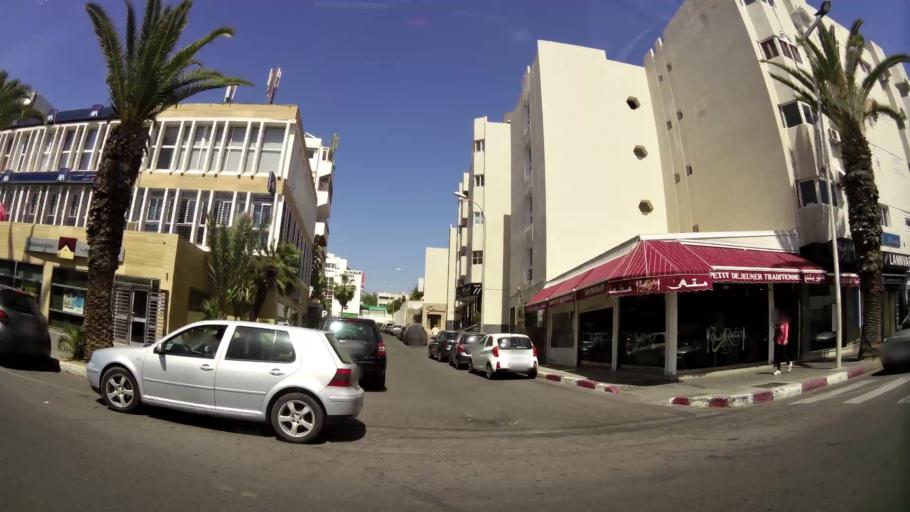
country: MA
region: Souss-Massa-Draa
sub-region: Agadir-Ida-ou-Tnan
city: Agadir
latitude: 30.4158
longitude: -9.5949
